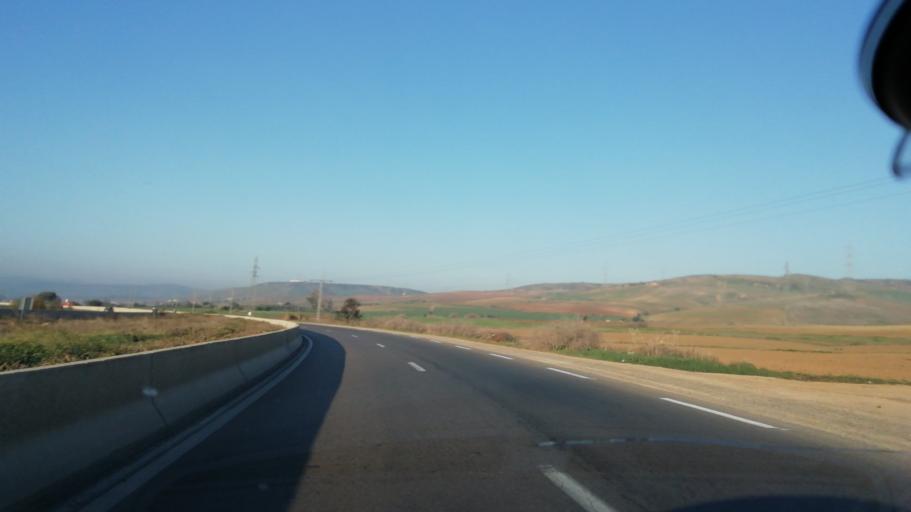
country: DZ
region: Ain Temouchent
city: Beni Saf
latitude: 35.2306
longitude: -1.3783
